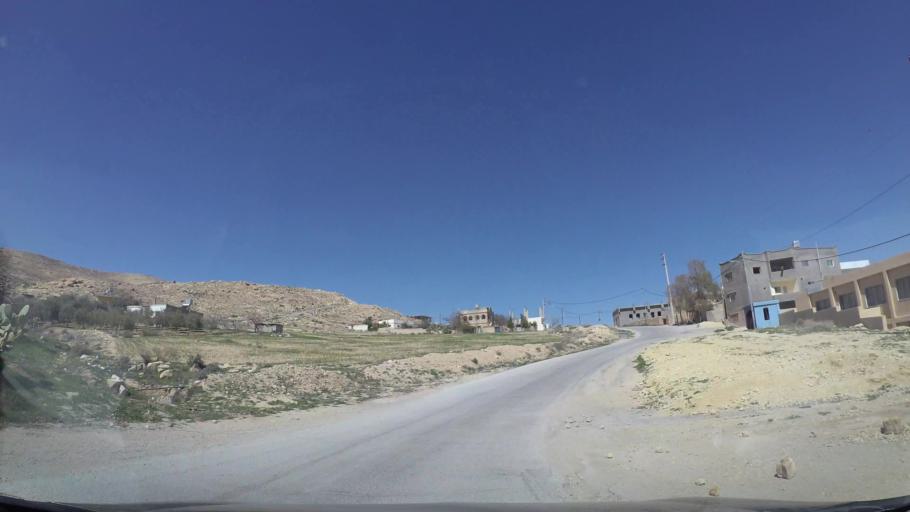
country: JO
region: Tafielah
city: At Tafilah
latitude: 30.8315
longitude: 35.5774
